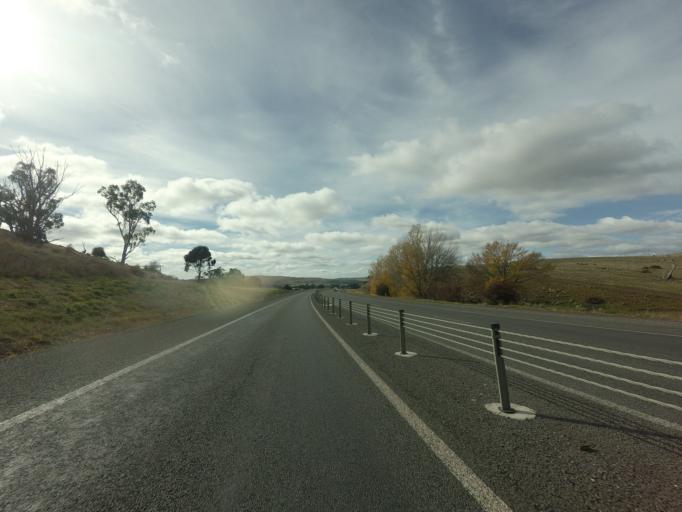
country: AU
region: Tasmania
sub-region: Brighton
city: Bridgewater
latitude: -42.3912
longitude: 147.2783
